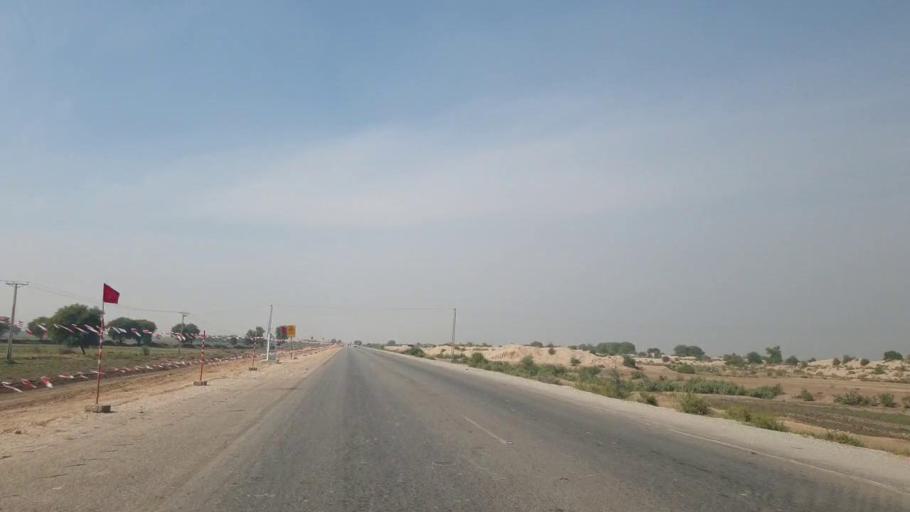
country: PK
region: Sindh
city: Sann
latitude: 25.9909
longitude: 68.1752
